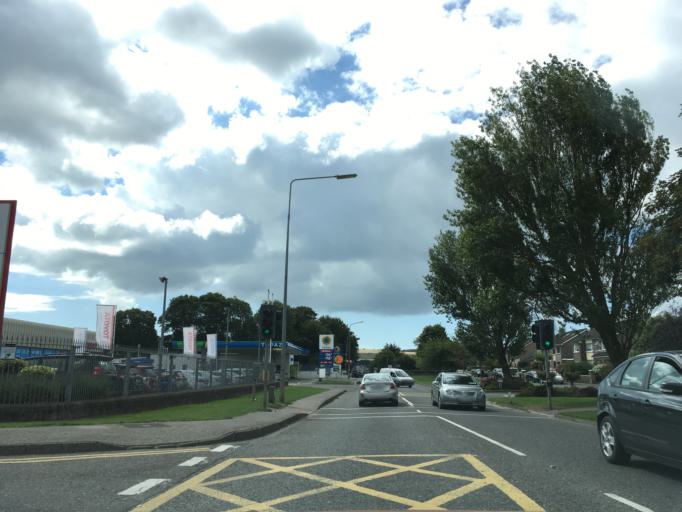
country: IE
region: Munster
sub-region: County Cork
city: Carrigaline
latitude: 51.8208
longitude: -8.3923
